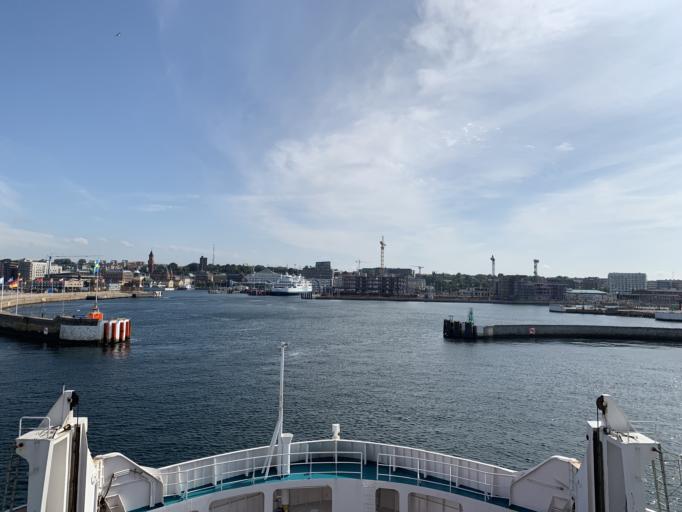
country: SE
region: Skane
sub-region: Helsingborg
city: Helsingborg
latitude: 56.0402
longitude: 12.6836
